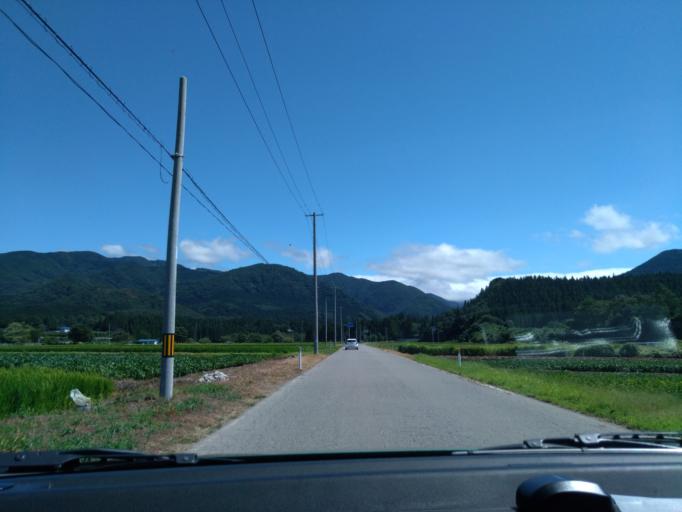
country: JP
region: Akita
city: Kakunodatemachi
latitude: 39.5309
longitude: 140.6390
